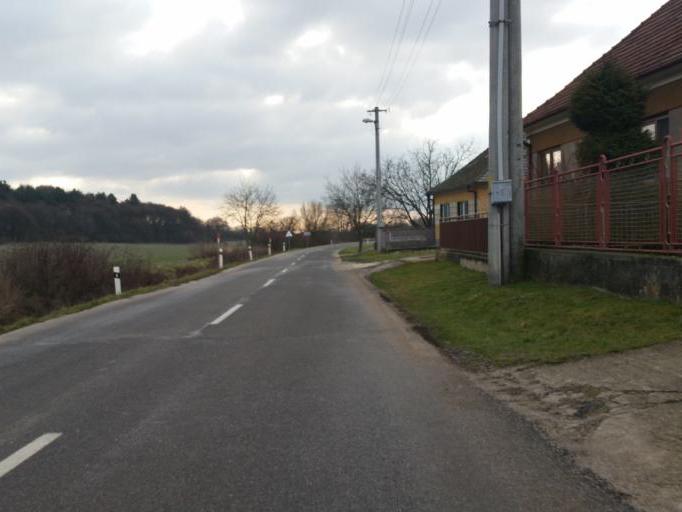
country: SK
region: Trnavsky
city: Vrbove
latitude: 48.6513
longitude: 17.7180
